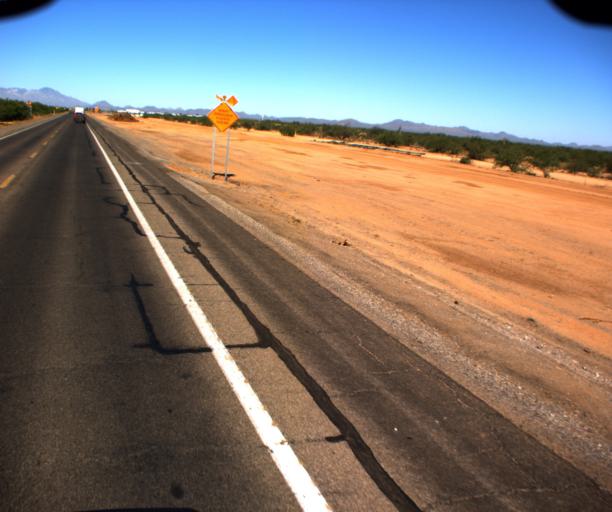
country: US
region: Arizona
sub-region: Pima County
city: Valencia West
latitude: 32.1408
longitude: -111.1499
